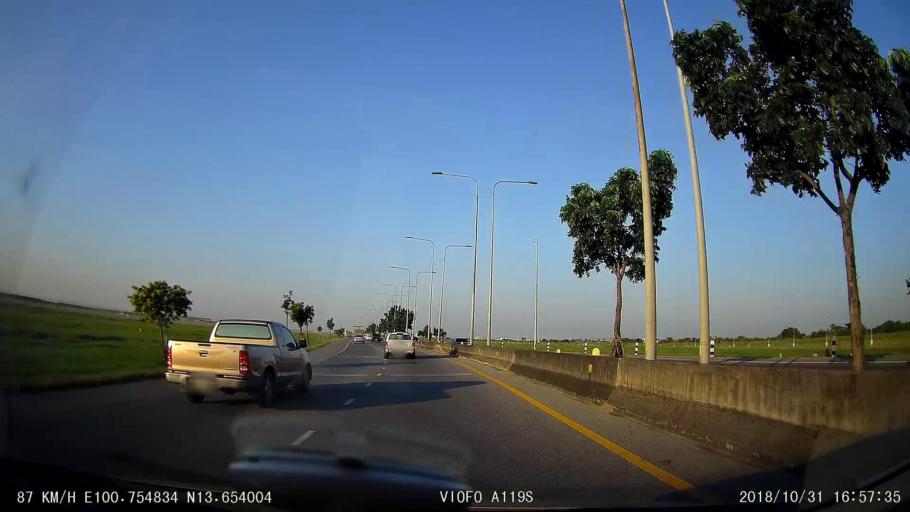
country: TH
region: Bangkok
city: Lat Krabang
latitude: 13.6541
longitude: 100.7549
